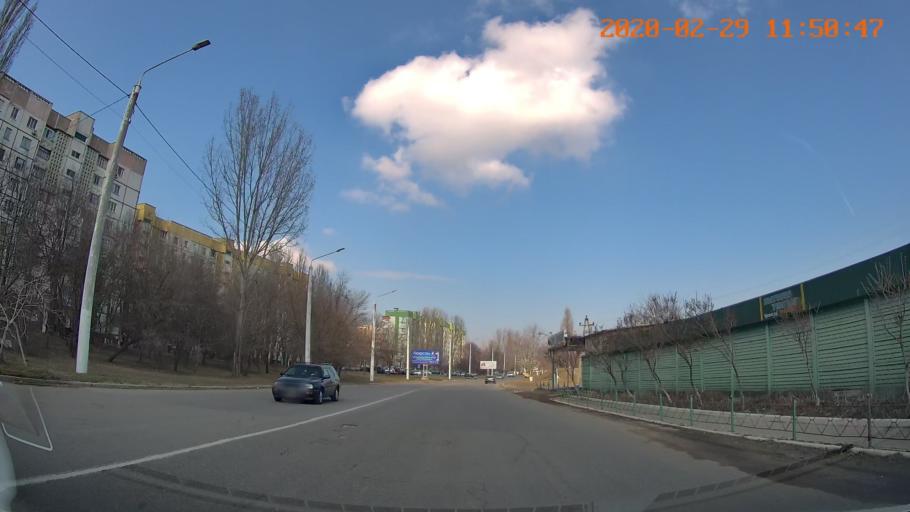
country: MD
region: Telenesti
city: Ribnita
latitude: 47.7608
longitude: 28.9898
